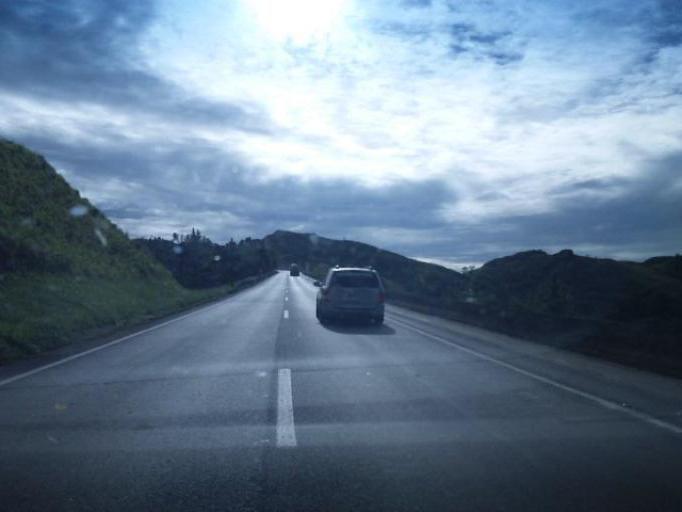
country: BR
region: Parana
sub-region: Campina Grande Do Sul
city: Campina Grande do Sul
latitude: -25.1011
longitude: -48.8286
